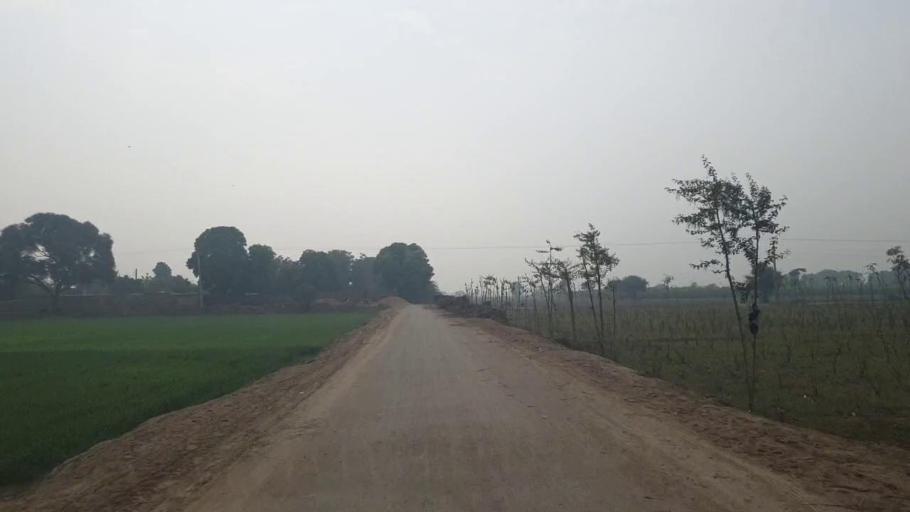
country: PK
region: Sindh
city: Tando Adam
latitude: 25.7052
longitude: 68.6263
